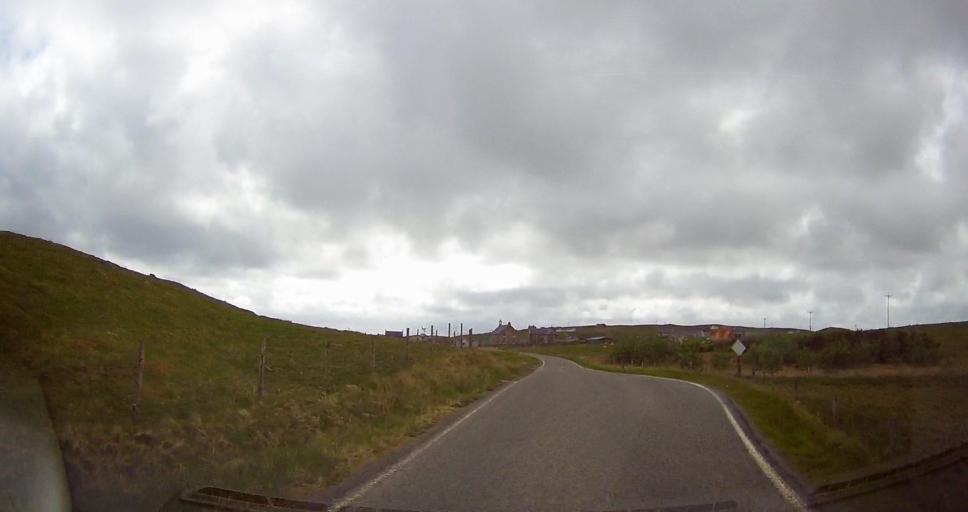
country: GB
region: Scotland
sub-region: Shetland Islands
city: Sandwick
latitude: 60.2323
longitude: -1.5573
